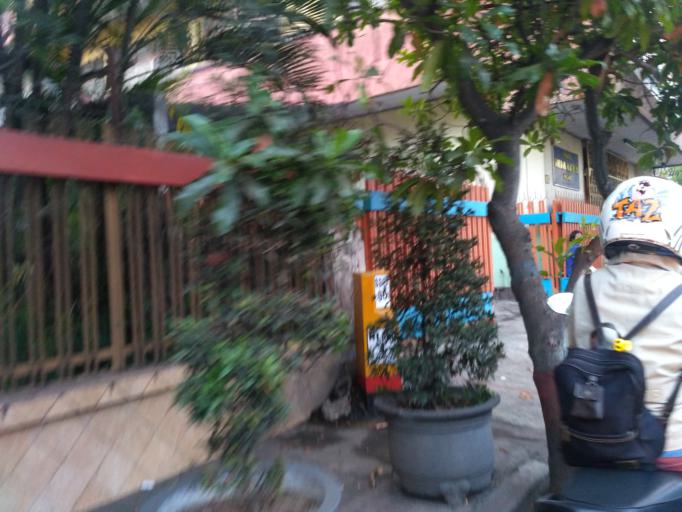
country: ID
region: East Java
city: Malang
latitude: -7.9914
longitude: 112.6341
